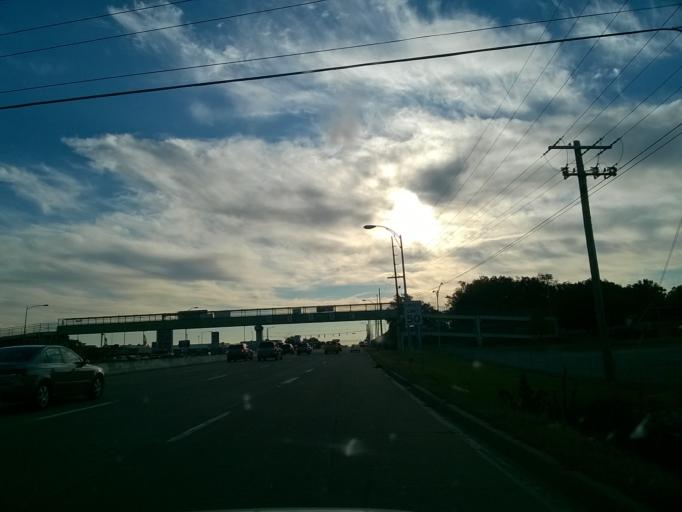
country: US
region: Indiana
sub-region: Vanderburgh County
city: Melody Hill
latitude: 37.9766
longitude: -87.4865
